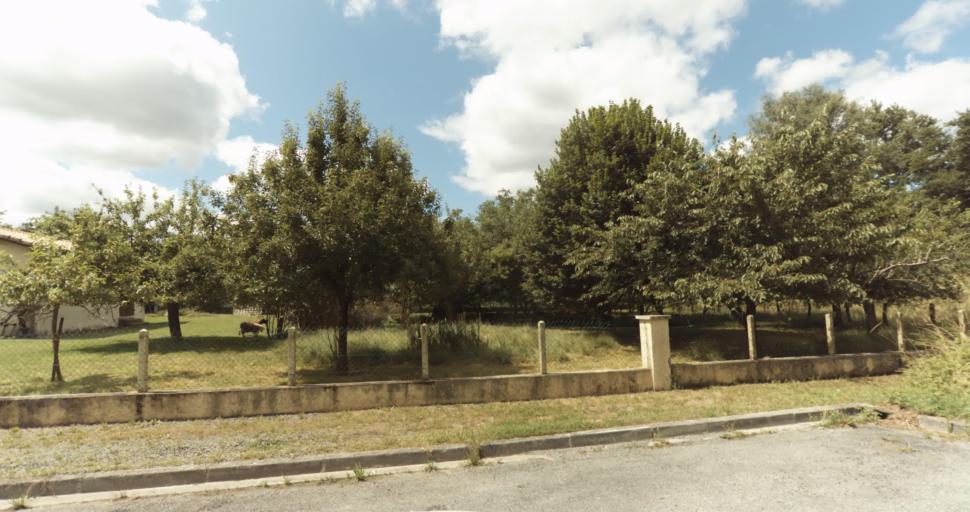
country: FR
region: Aquitaine
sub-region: Departement de la Gironde
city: Bazas
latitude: 44.4400
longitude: -0.2243
